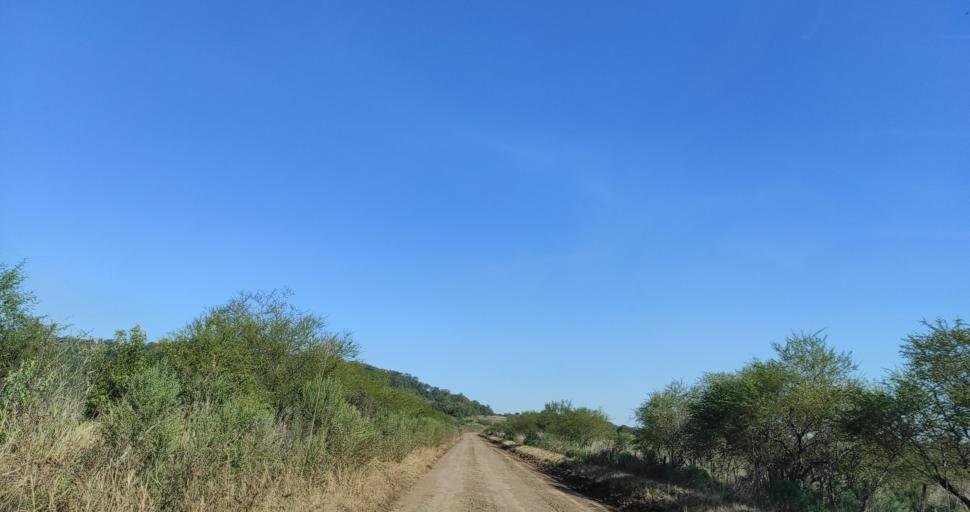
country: AR
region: Misiones
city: Cerro Cora
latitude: -27.6627
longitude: -55.6594
